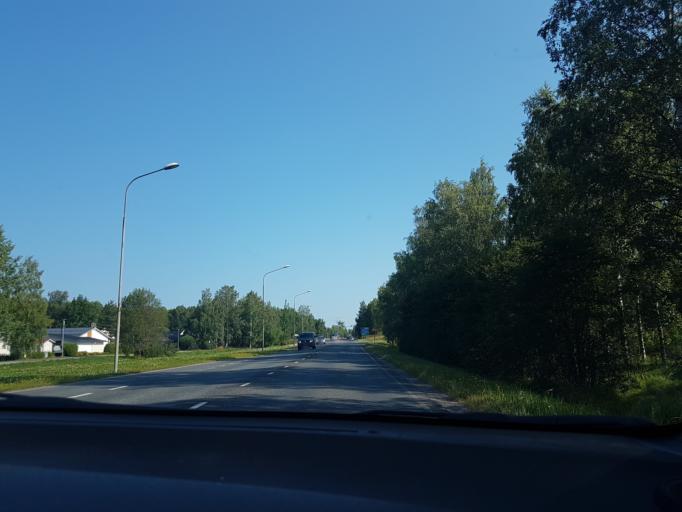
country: FI
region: Uusimaa
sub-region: Helsinki
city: Kerava
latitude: 60.3915
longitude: 25.1009
